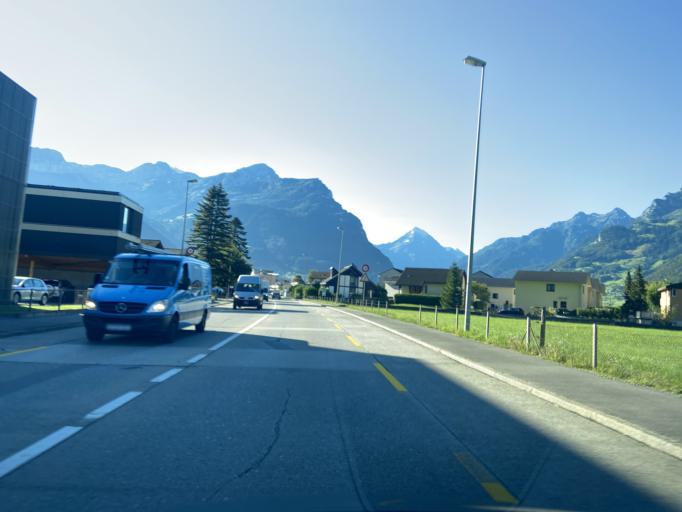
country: CH
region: Uri
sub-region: Uri
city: Flueelen
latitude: 46.8917
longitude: 8.6278
